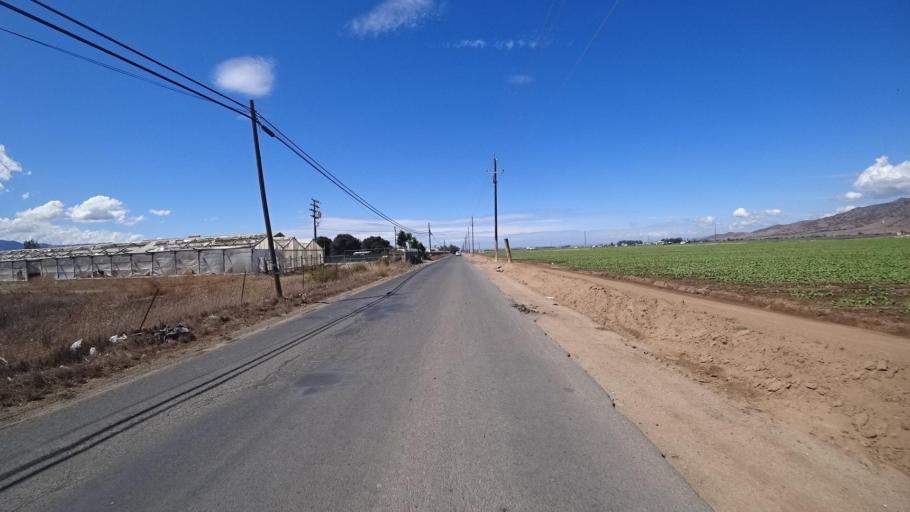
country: US
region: California
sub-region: Monterey County
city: Chualar
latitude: 36.6224
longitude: -121.5120
